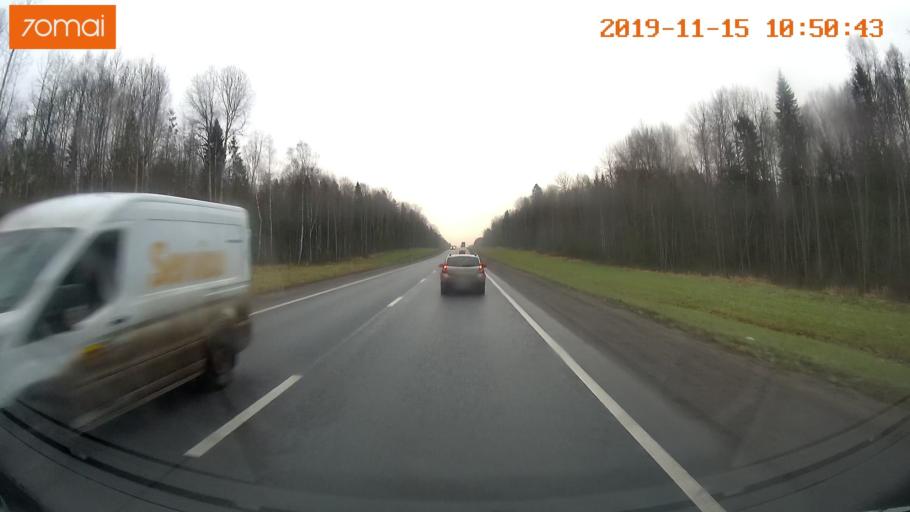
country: RU
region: Vologda
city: Chebsara
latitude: 59.1839
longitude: 38.6880
